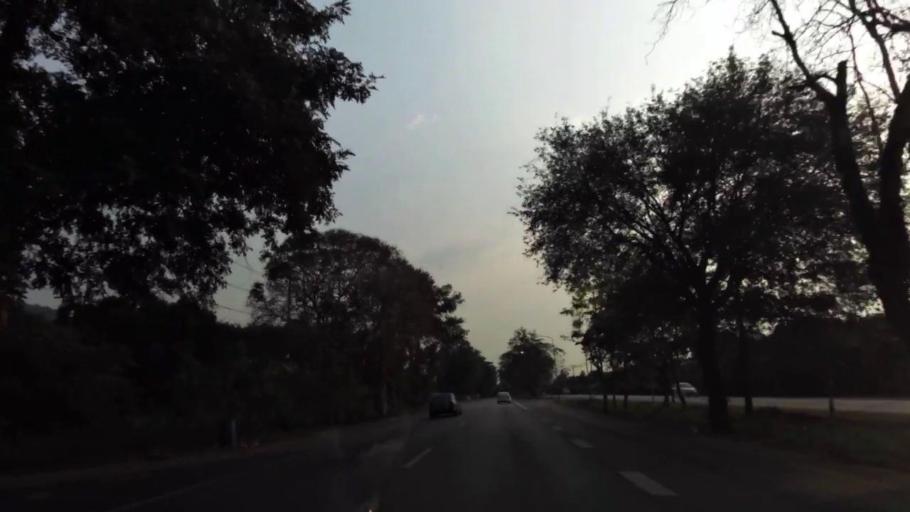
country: TH
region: Chanthaburi
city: Chanthaburi
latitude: 12.5678
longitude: 102.1619
